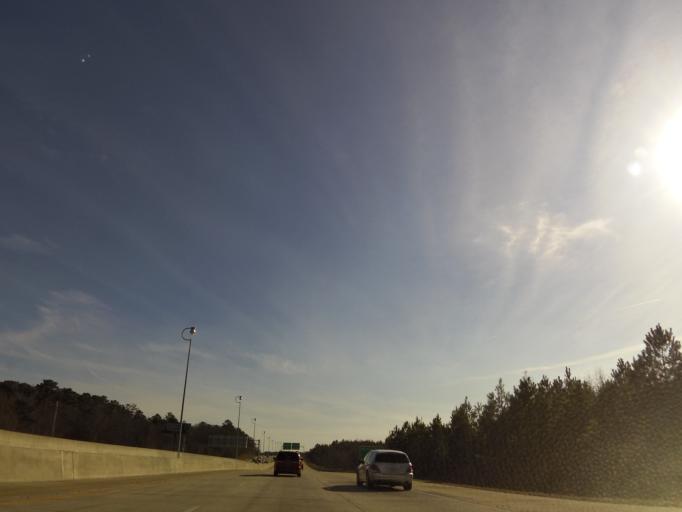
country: US
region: Georgia
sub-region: Muscogee County
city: Columbus
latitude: 32.4212
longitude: -84.9281
